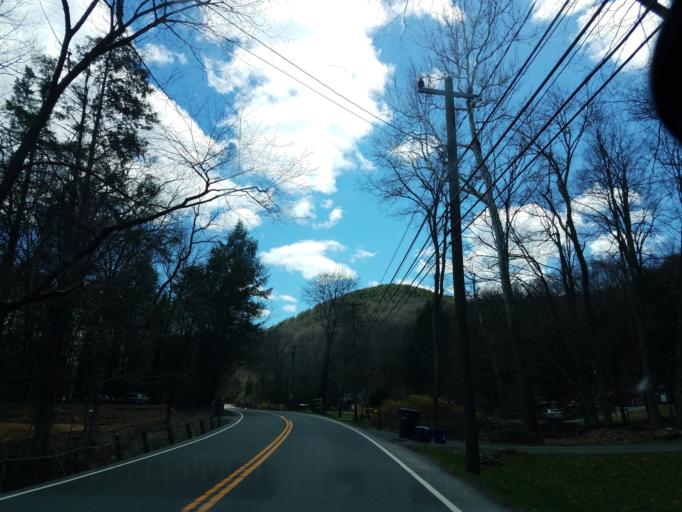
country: US
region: Connecticut
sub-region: Fairfield County
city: Sherman
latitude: 41.6358
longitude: -73.4765
